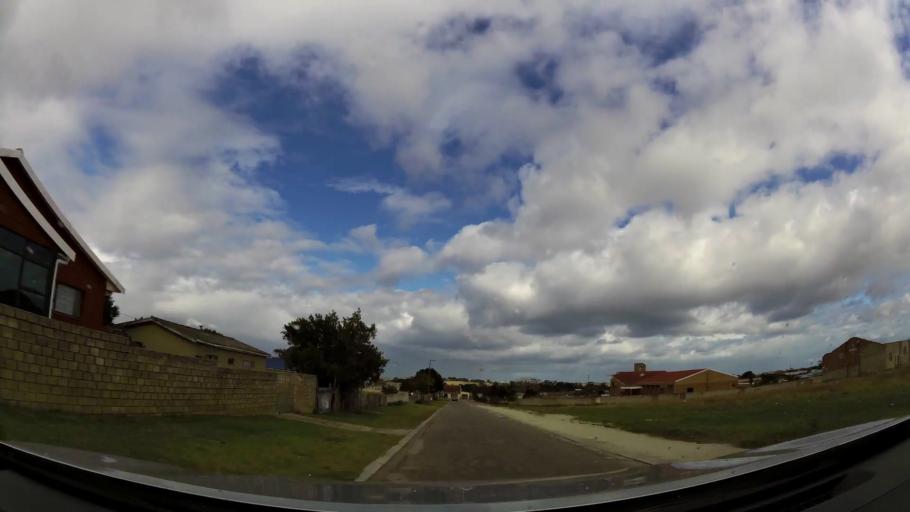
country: ZA
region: Western Cape
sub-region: Eden District Municipality
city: George
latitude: -34.0208
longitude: 22.4672
